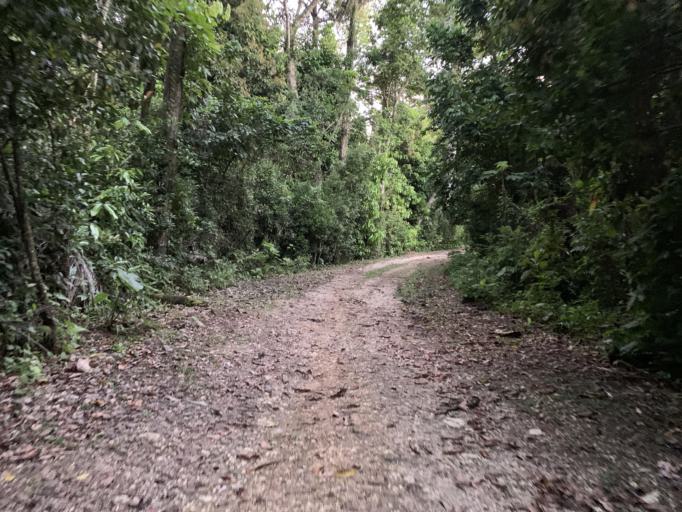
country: PR
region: San Sebastian
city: Juncal
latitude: 18.3704
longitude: -66.9194
